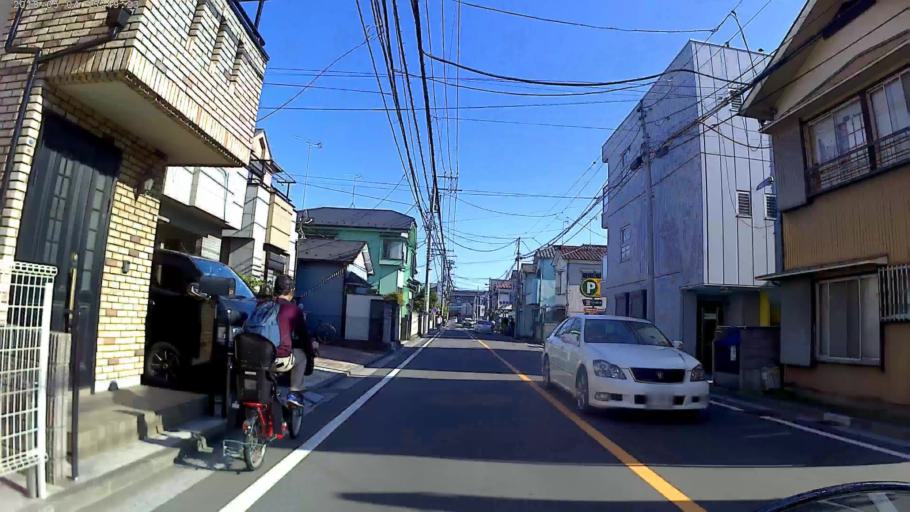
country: JP
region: Kanagawa
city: Yokohama
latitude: 35.4977
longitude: 139.6463
